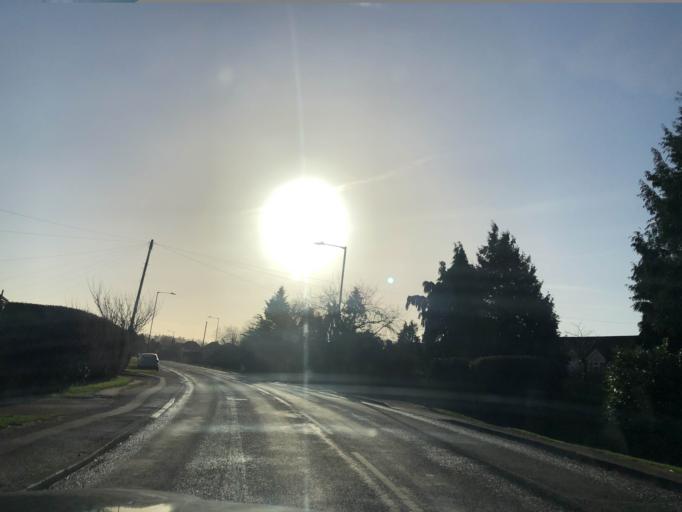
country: GB
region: England
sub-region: Warwickshire
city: Wellesbourne Mountford
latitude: 52.1929
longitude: -1.5872
